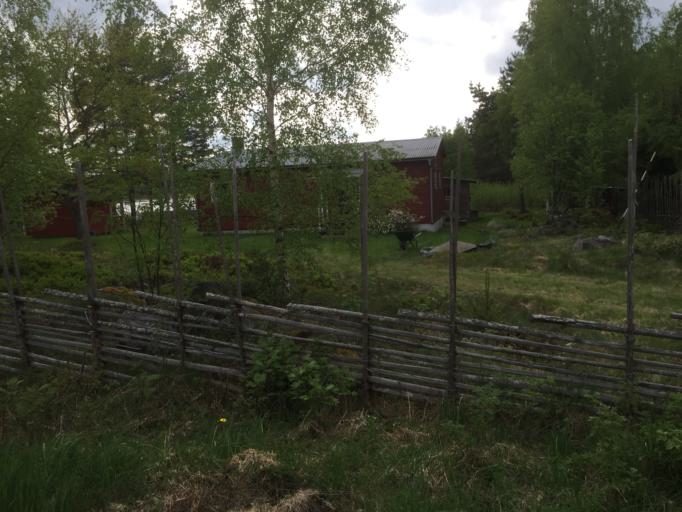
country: SE
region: Uppsala
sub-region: Alvkarleby Kommun
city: Skutskaer
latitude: 60.7916
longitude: 17.2968
